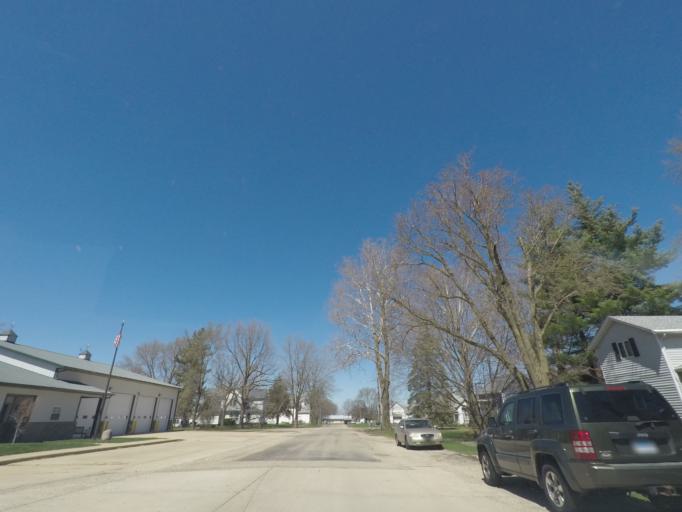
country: US
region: Illinois
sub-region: Macon County
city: Warrensburg
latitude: 39.9669
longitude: -89.1615
